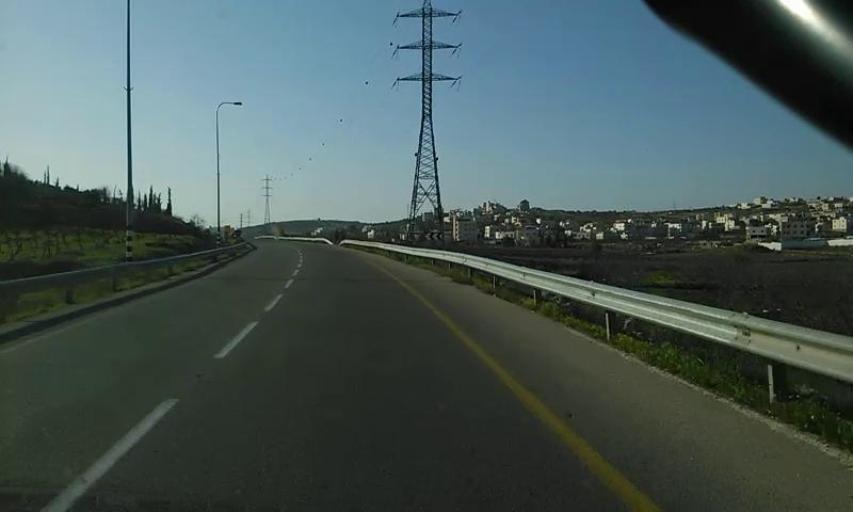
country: PS
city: Bayt `Inun
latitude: 31.5592
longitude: 35.1317
